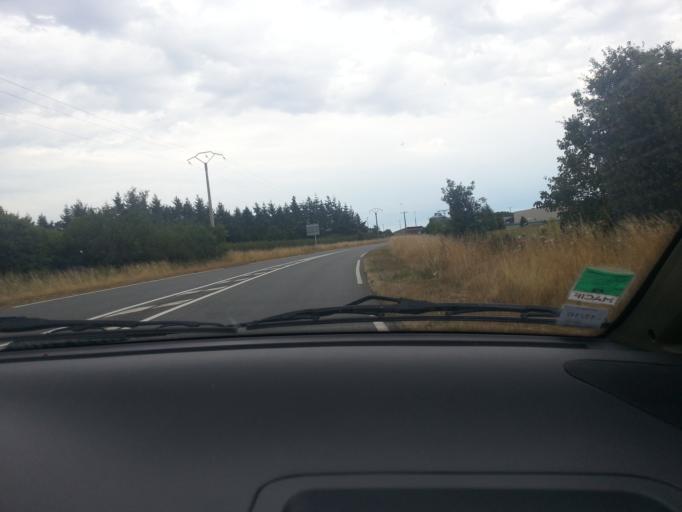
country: FR
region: Auvergne
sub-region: Departement de l'Allier
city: Saint-Gerand-le-Puy
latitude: 46.2080
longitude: 3.5021
